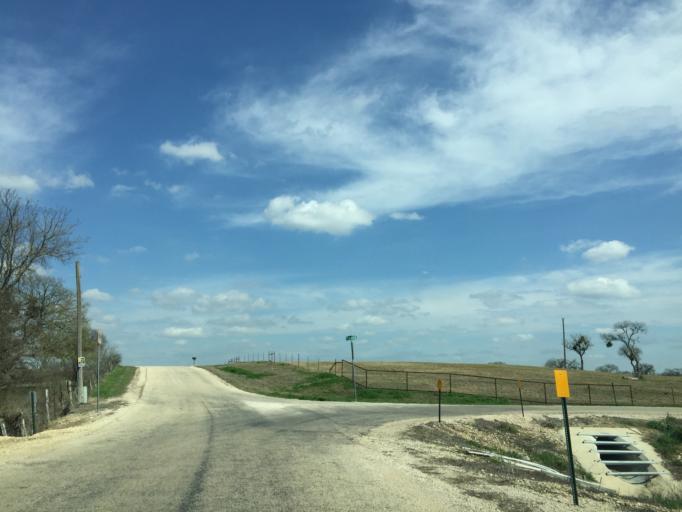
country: US
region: Texas
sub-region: Milam County
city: Thorndale
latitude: 30.5541
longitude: -97.2182
